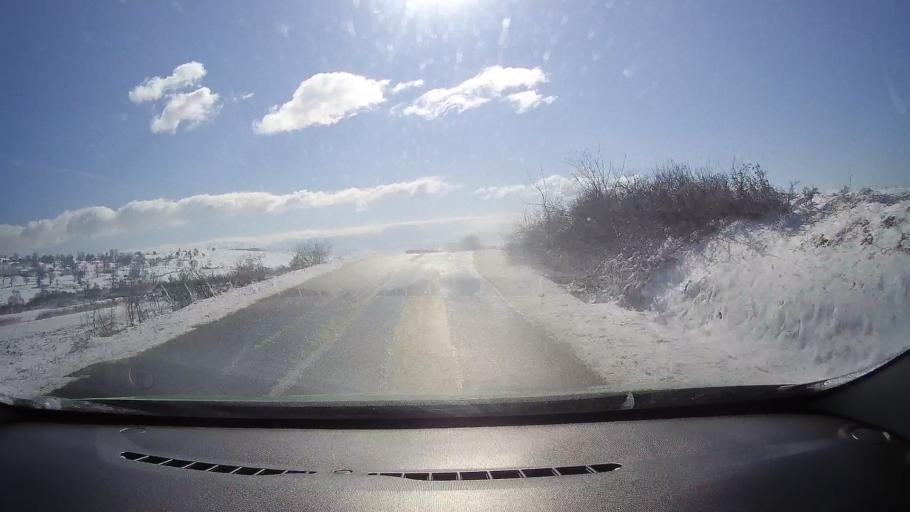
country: RO
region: Sibiu
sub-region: Comuna Rosia
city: Rosia
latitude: 45.8531
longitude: 24.3094
